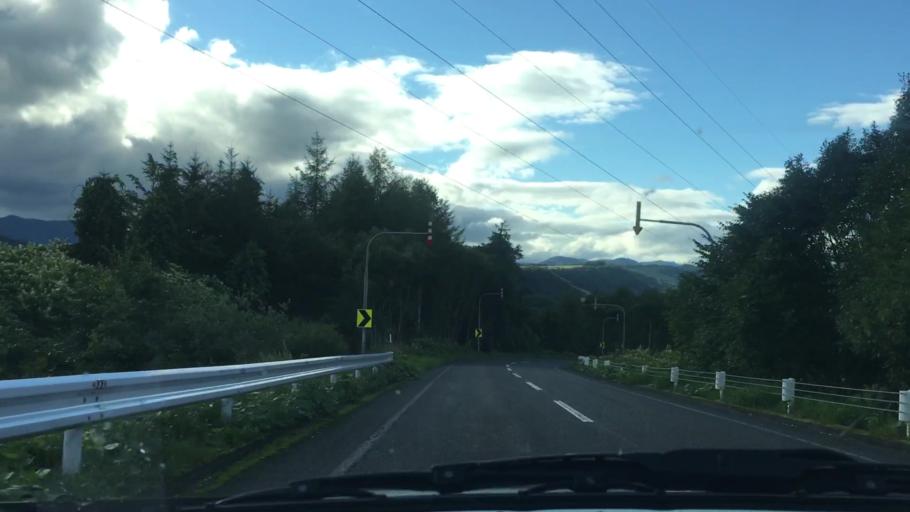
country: JP
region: Hokkaido
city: Otofuke
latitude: 43.1737
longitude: 142.9306
